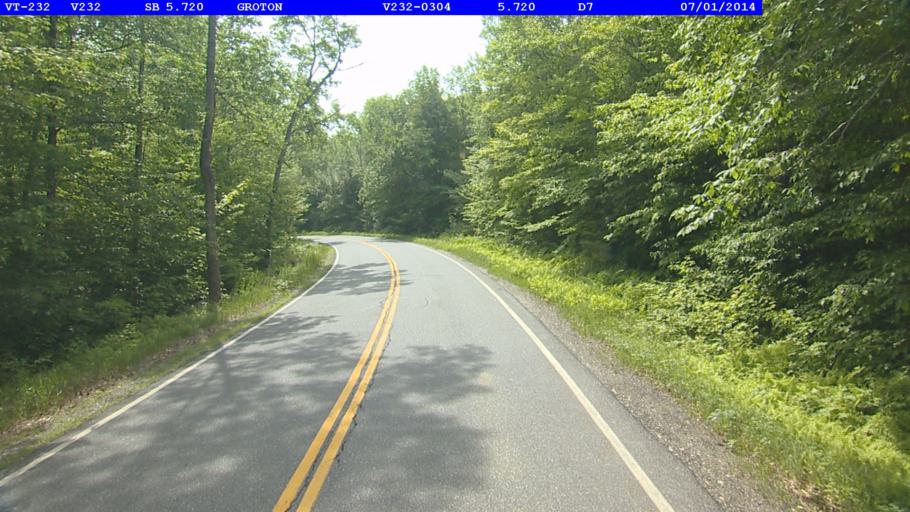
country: US
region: Vermont
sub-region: Washington County
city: Barre
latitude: 44.2799
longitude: -72.2897
